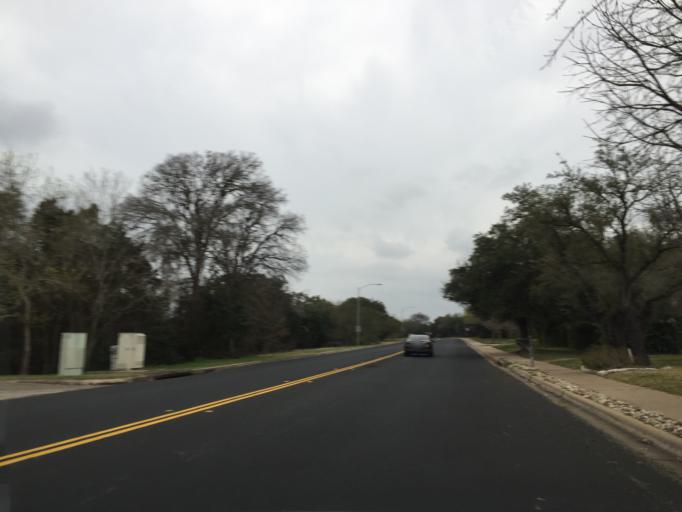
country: US
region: Texas
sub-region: Travis County
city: Rollingwood
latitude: 30.2426
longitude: -97.8280
